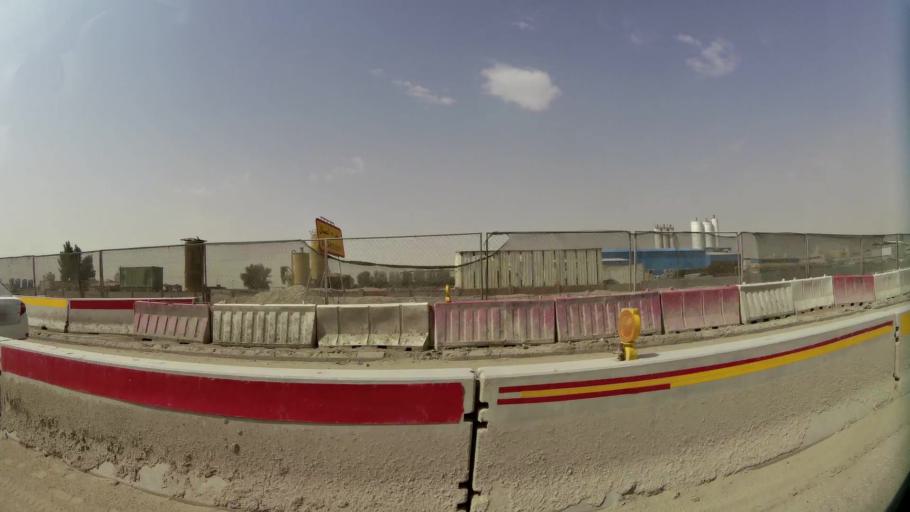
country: QA
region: Al Wakrah
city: Al Wukayr
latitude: 25.1648
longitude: 51.4538
